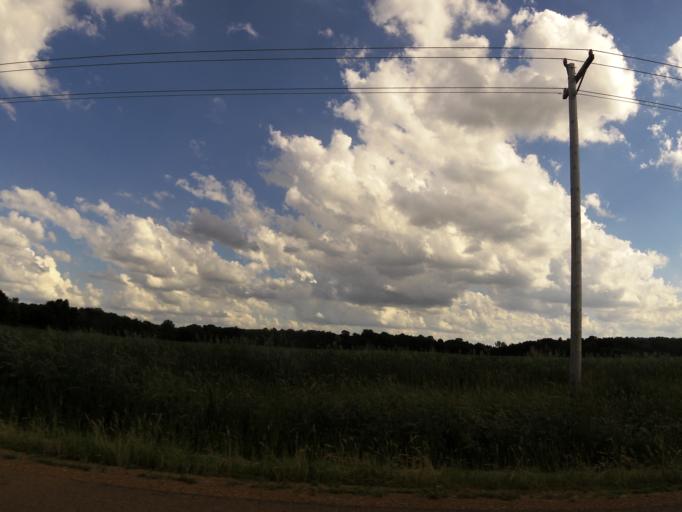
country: US
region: Minnesota
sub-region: Carver County
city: Waconia
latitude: 44.8292
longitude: -93.7522
